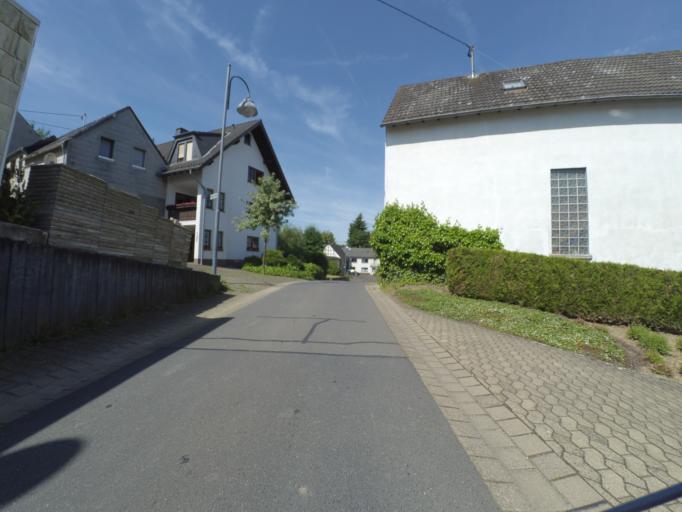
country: DE
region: Rheinland-Pfalz
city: Eppenberg
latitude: 50.2488
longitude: 7.0740
